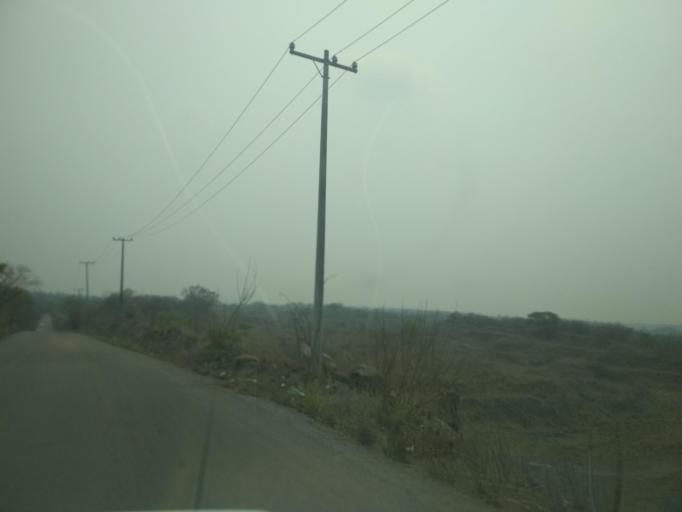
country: MX
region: Veracruz
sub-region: Veracruz
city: Delfino Victoria (Santa Fe)
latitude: 19.1866
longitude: -96.3164
